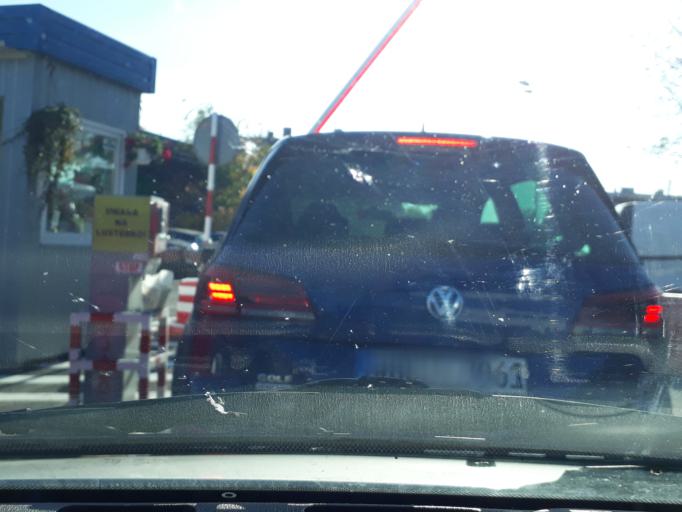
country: PL
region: Silesian Voivodeship
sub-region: Powiat tarnogorski
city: Tarnowskie Gory
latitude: 50.4445
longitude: 18.8627
